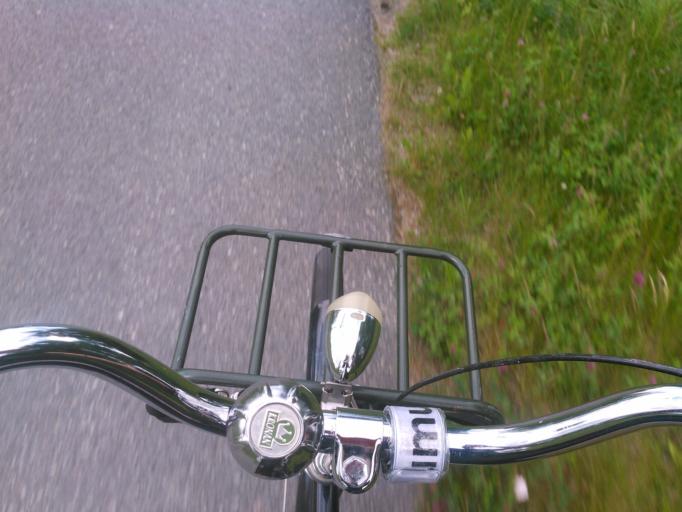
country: SE
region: Vaesterbotten
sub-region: Umea Kommun
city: Umea
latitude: 63.8387
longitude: 20.2471
